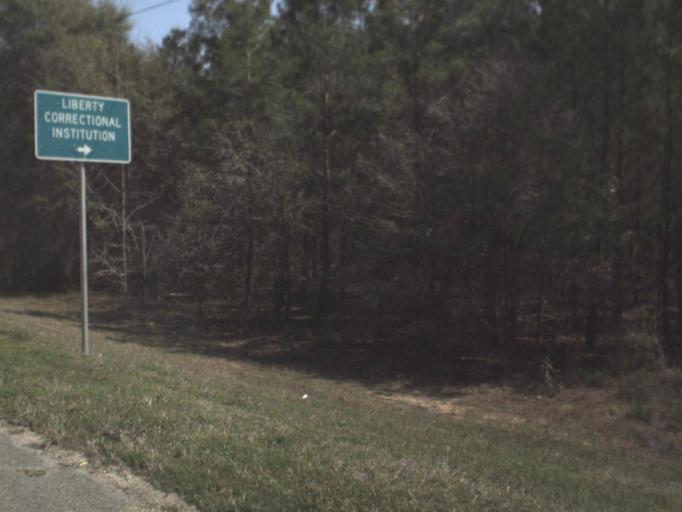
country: US
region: Florida
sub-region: Liberty County
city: Bristol
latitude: 30.4920
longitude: -84.8999
